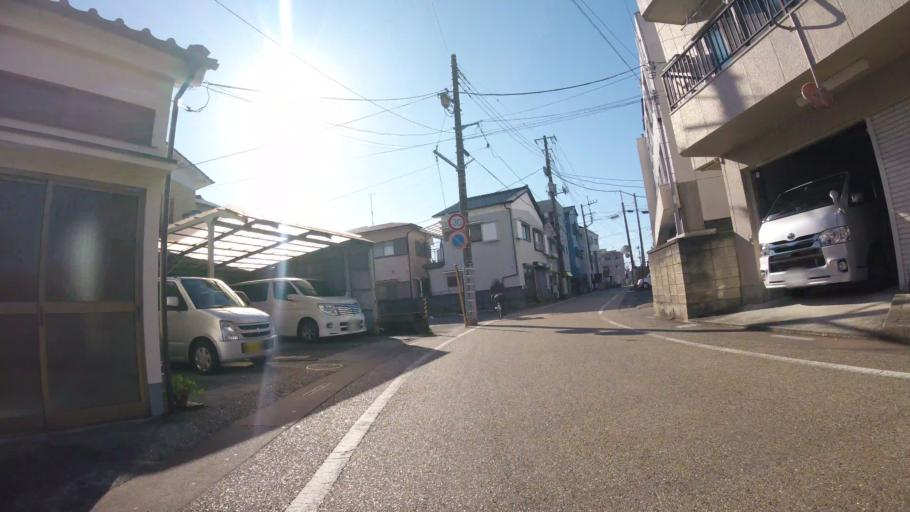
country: JP
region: Shizuoka
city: Mishima
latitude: 35.1200
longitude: 138.9105
